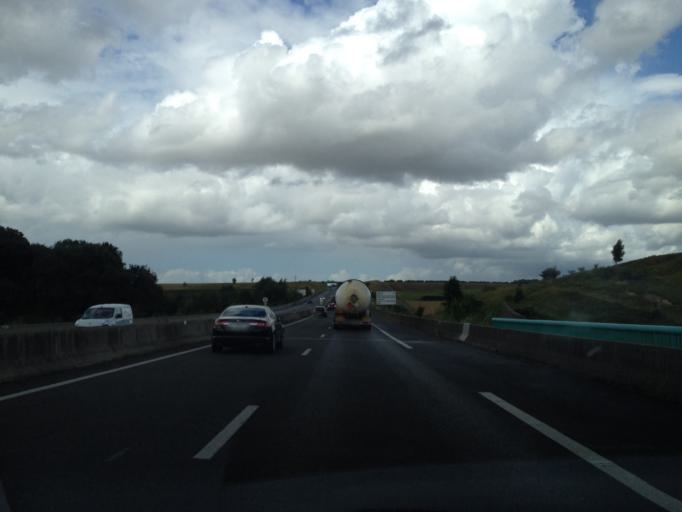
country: FR
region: Picardie
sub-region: Departement de la Somme
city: Sailly-Flibeaucourt
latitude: 50.1436
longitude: 1.8042
